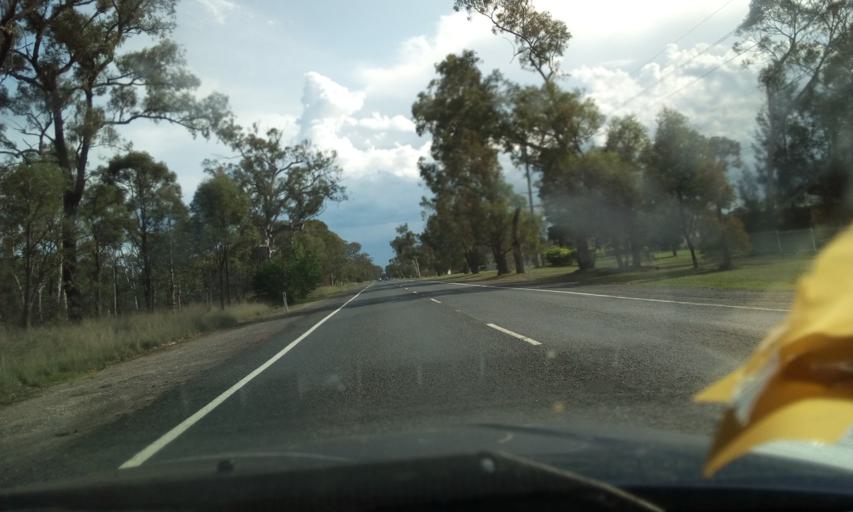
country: AU
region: New South Wales
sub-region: Hawkesbury
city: Richmond
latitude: -33.6717
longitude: 150.7514
